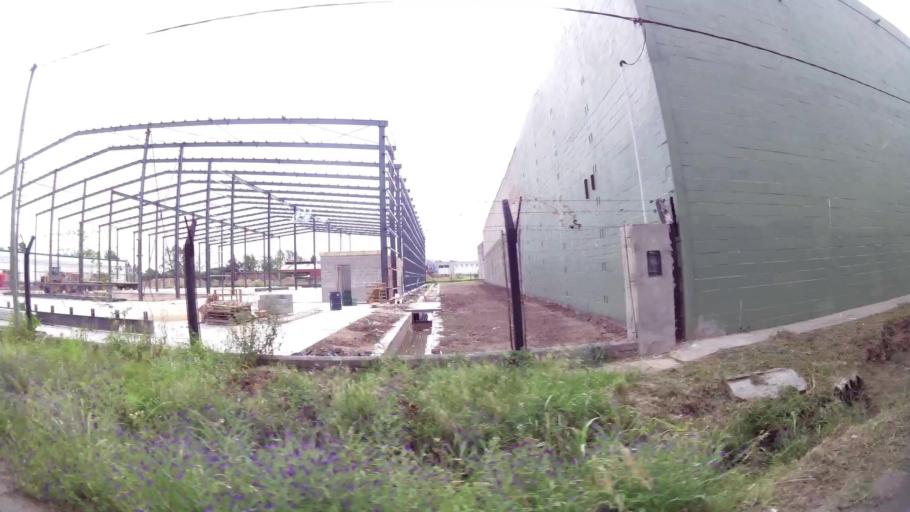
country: AR
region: Santa Fe
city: Gobernador Galvez
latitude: -33.0105
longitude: -60.6673
